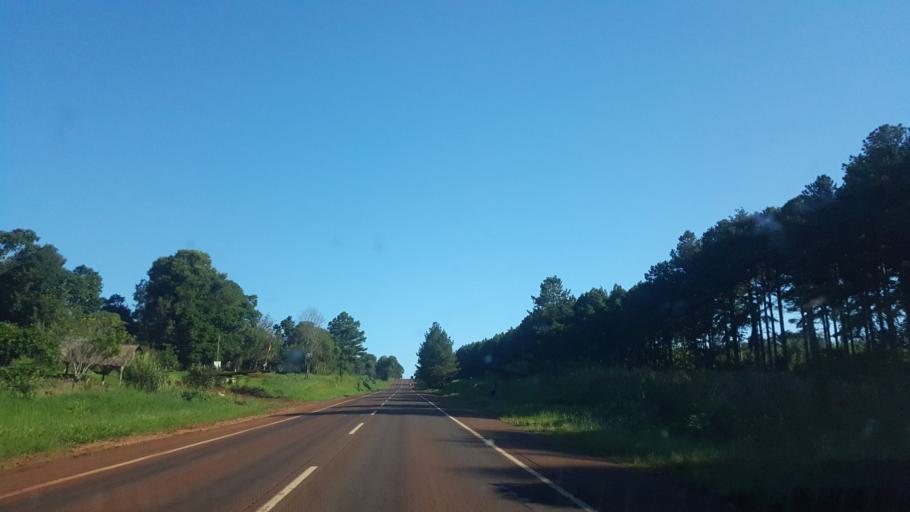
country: AR
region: Misiones
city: Puerto Esperanza
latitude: -26.1538
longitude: -54.5830
